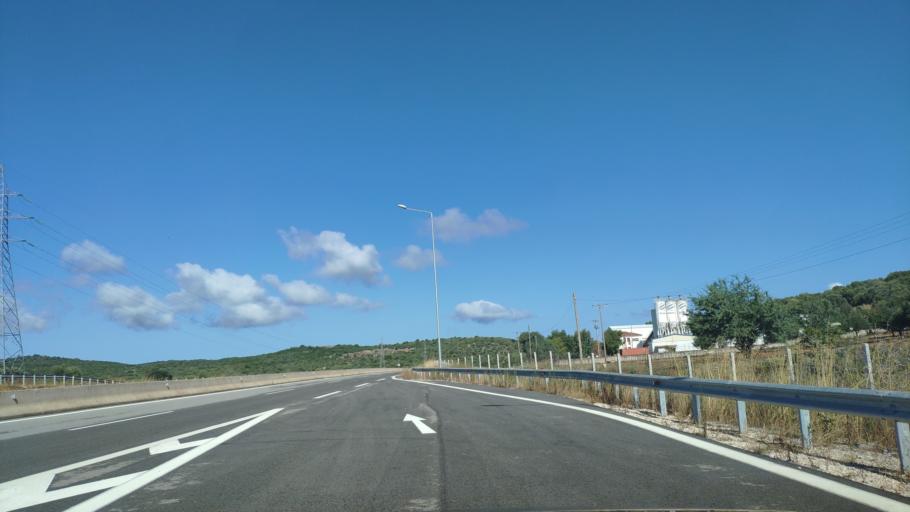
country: GR
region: West Greece
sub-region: Nomos Aitolias kai Akarnanias
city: Vonitsa
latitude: 38.9036
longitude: 20.8587
